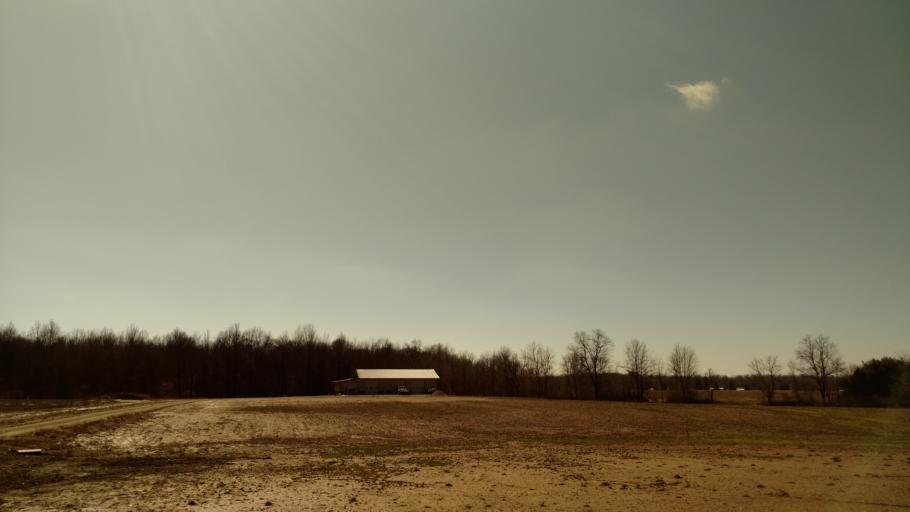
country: US
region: Ohio
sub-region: Morrow County
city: Cardington
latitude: 40.4978
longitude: -82.8591
